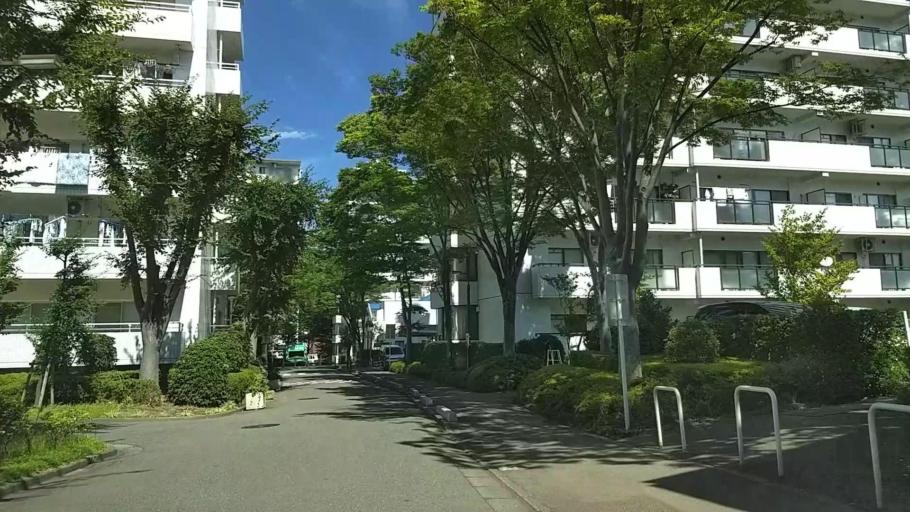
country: JP
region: Tokyo
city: Chofugaoka
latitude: 35.5654
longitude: 139.5677
